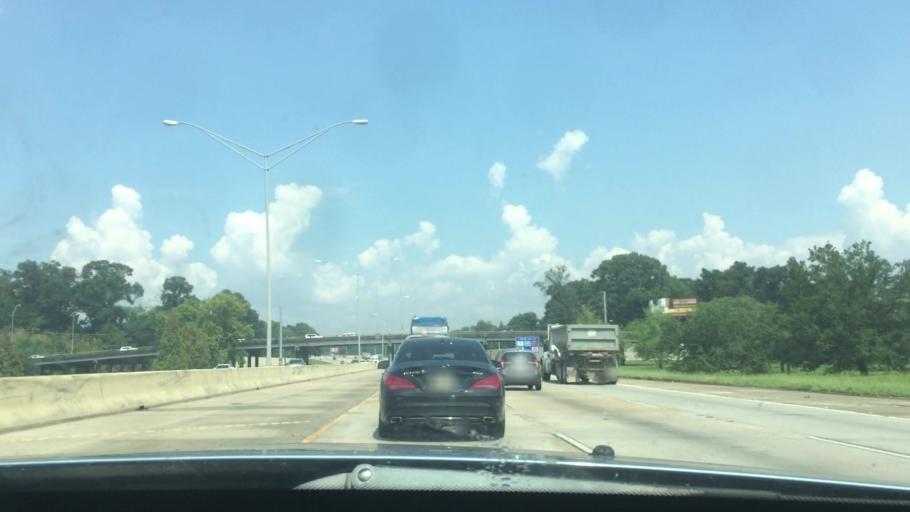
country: US
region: Louisiana
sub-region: East Baton Rouge Parish
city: Westminster
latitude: 30.4173
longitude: -91.0999
